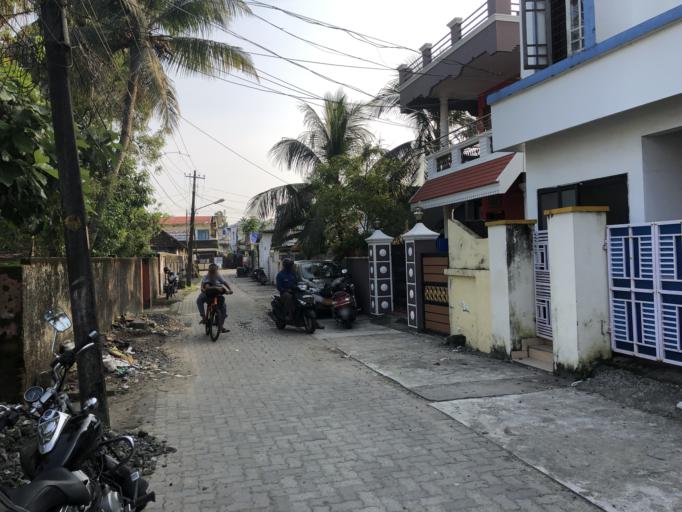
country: IN
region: Kerala
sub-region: Ernakulam
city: Cochin
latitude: 9.9616
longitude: 76.2511
